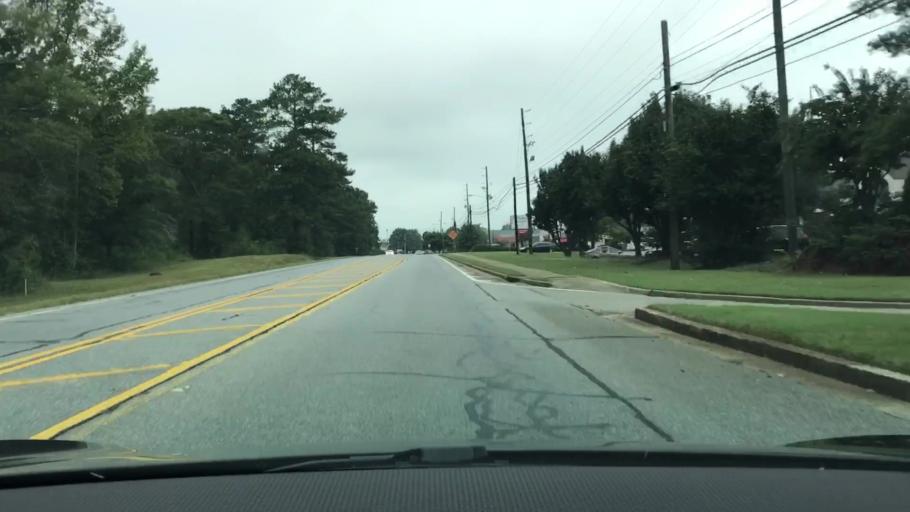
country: US
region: Georgia
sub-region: Oconee County
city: Watkinsville
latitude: 33.8720
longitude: -83.4354
